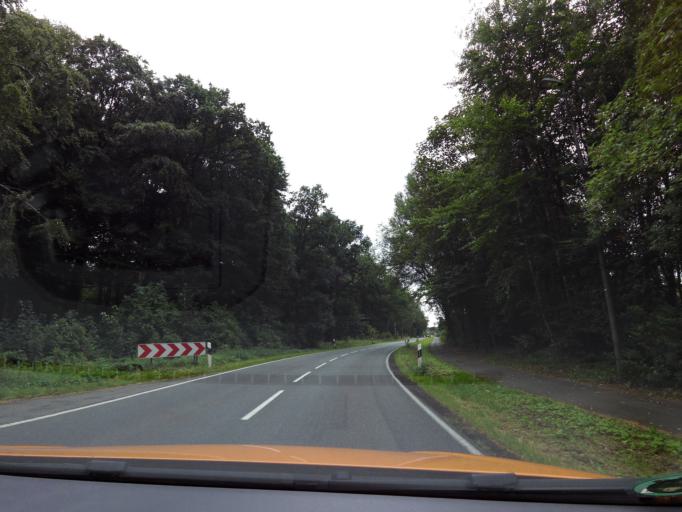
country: DE
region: Lower Saxony
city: Harpstedt
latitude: 52.9150
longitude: 8.6001
